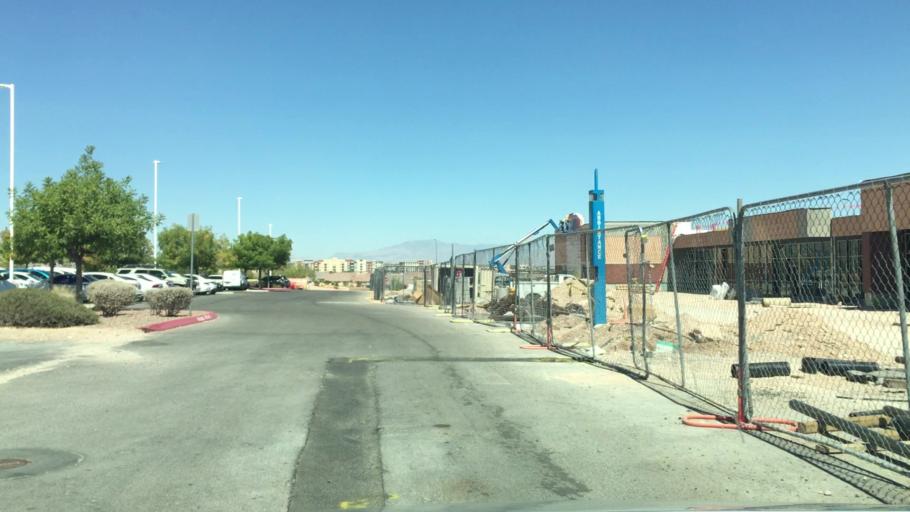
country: US
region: Nevada
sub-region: Clark County
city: Summerlin South
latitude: 36.0725
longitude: -115.2944
